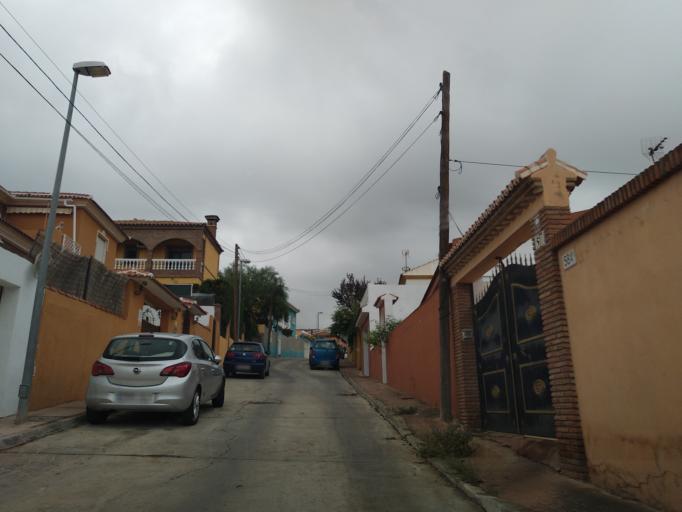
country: ES
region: Andalusia
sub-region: Provincia de Malaga
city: Malaga
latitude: 36.7462
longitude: -4.4771
